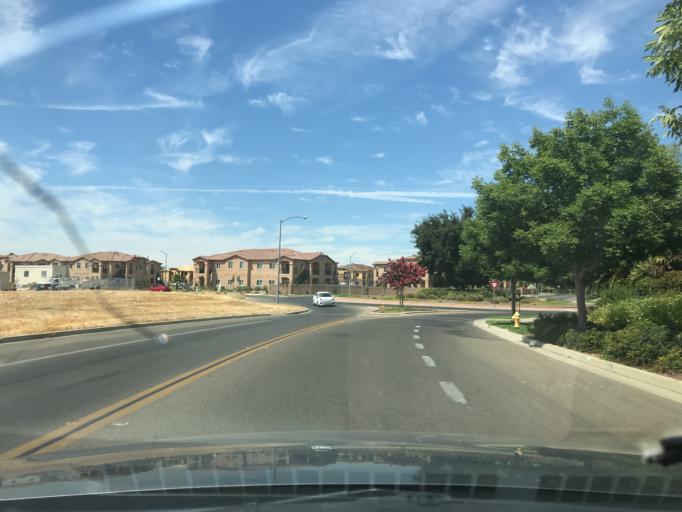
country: US
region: California
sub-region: Merced County
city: Merced
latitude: 37.3358
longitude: -120.4886
